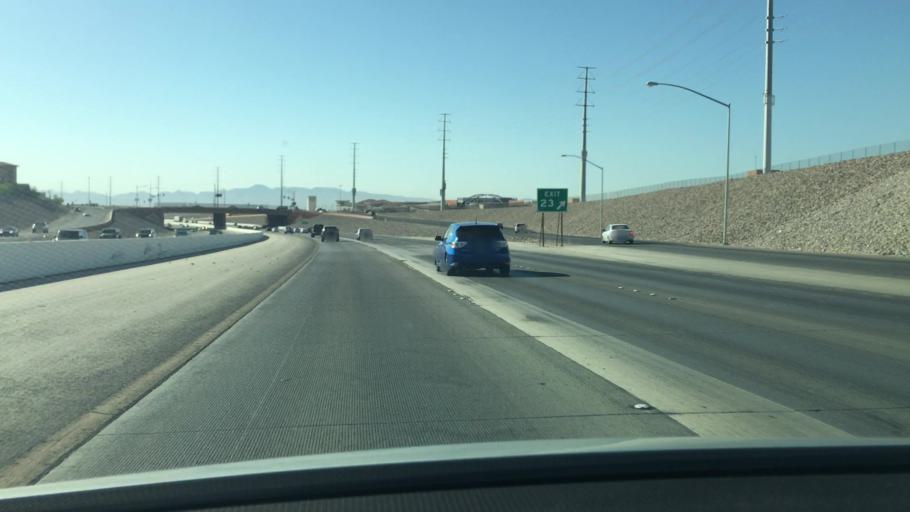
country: US
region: Nevada
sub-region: Clark County
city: Summerlin South
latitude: 36.1240
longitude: -115.3305
